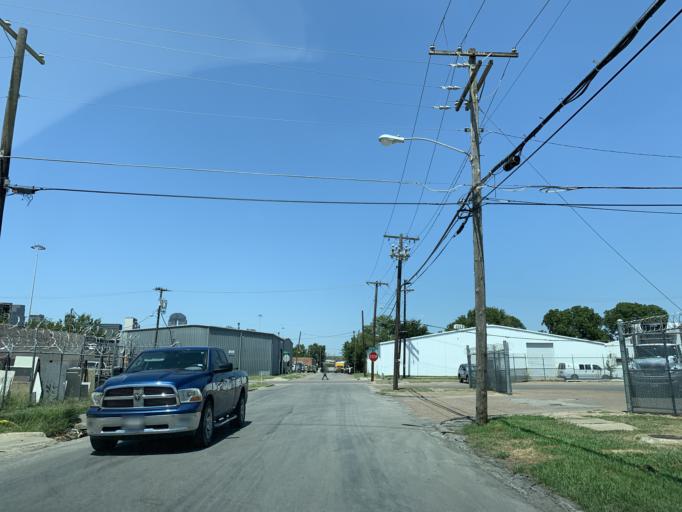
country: US
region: Texas
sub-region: Dallas County
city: Dallas
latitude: 32.7759
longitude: -96.7777
